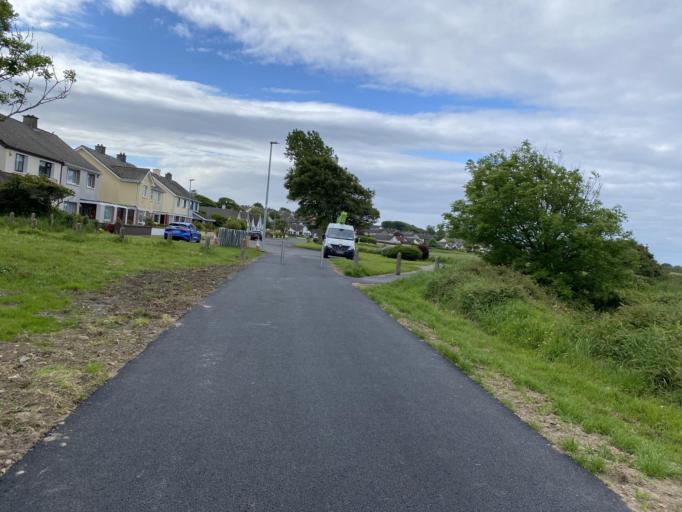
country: IE
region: Connaught
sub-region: County Galway
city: Gaillimh
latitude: 53.2788
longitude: -9.0296
